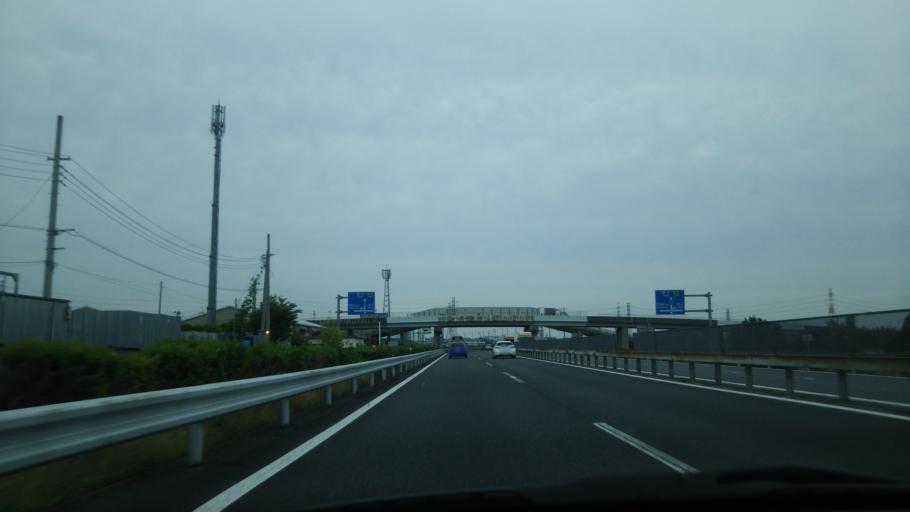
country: JP
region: Kanagawa
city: Isehara
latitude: 35.3895
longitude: 139.3326
